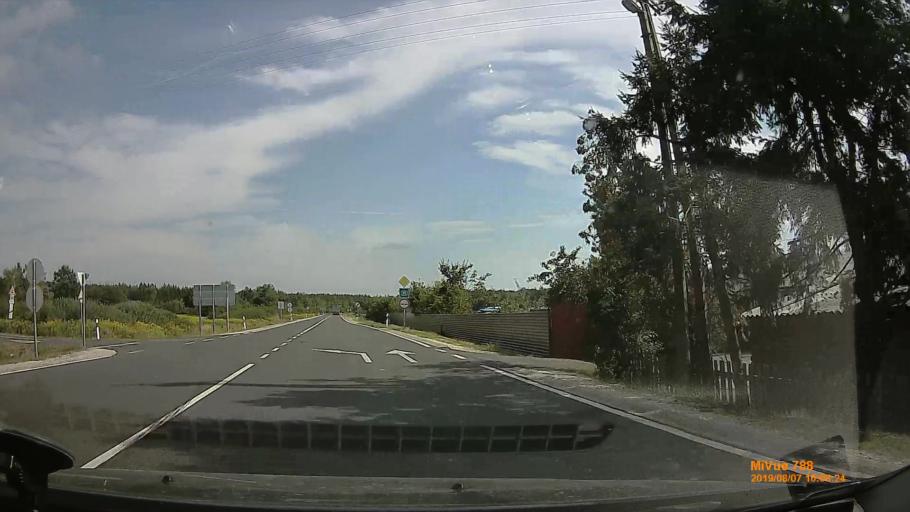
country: HU
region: Zala
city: Zalalovo
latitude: 46.9089
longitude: 16.6022
